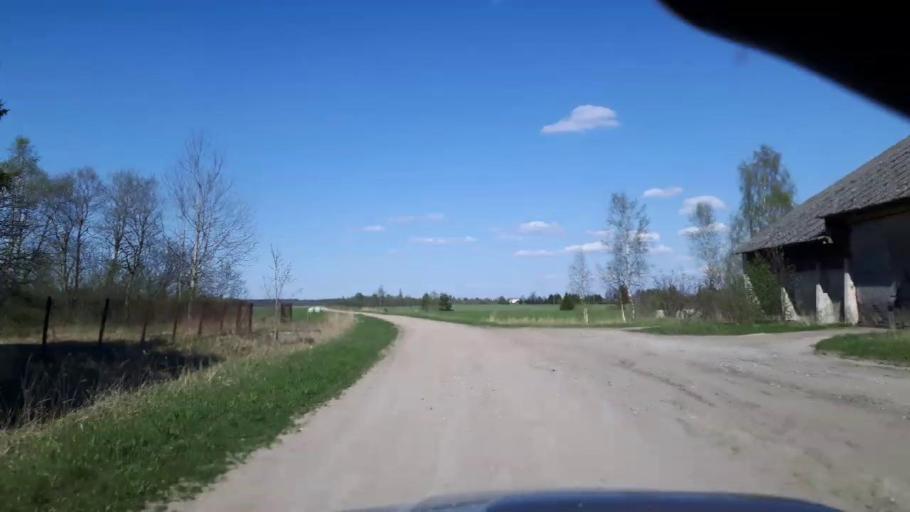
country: EE
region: Paernumaa
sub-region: Tootsi vald
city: Tootsi
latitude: 58.5258
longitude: 24.8225
